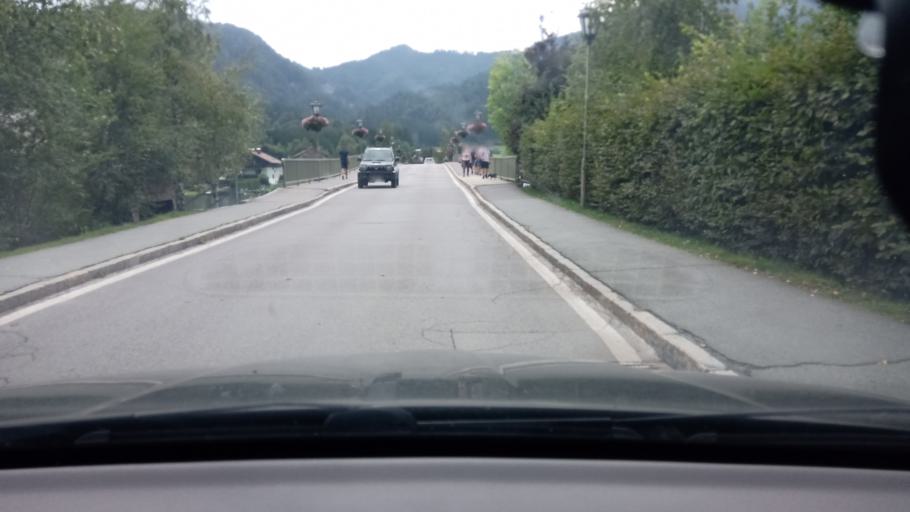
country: AT
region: Carinthia
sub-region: Politischer Bezirk Spittal an der Drau
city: Steinfeld
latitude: 46.7164
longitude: 13.2946
